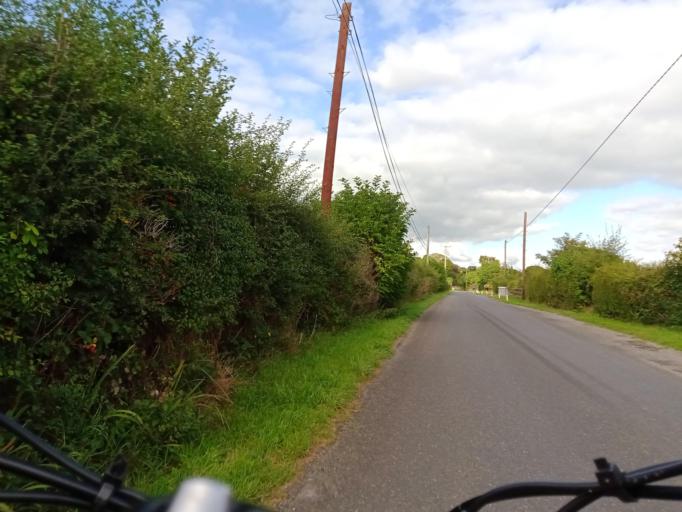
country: IE
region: Leinster
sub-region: Kilkenny
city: Kilkenny
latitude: 52.6116
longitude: -7.2127
